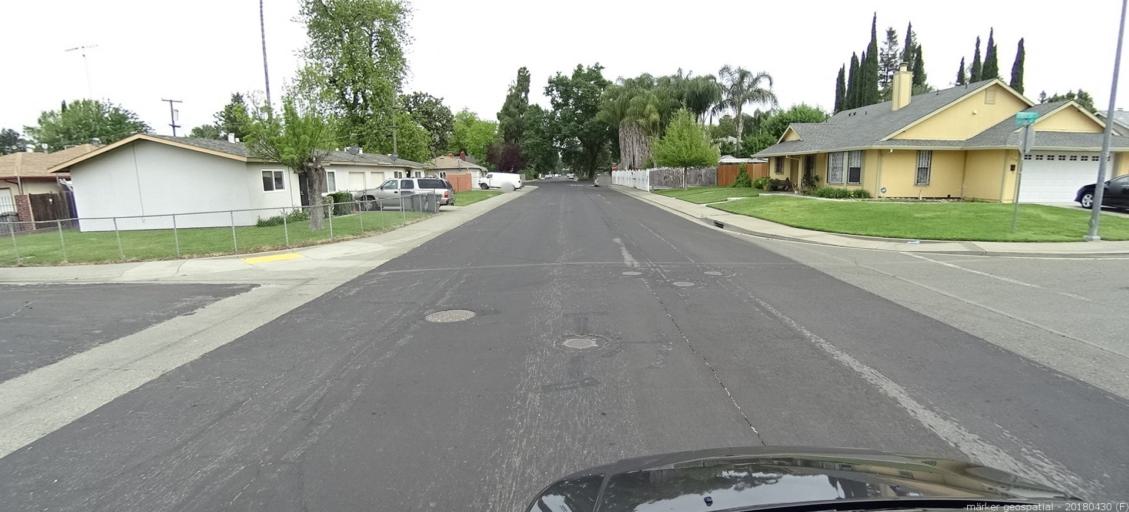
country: US
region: California
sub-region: Yolo County
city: West Sacramento
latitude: 38.5954
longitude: -121.5362
